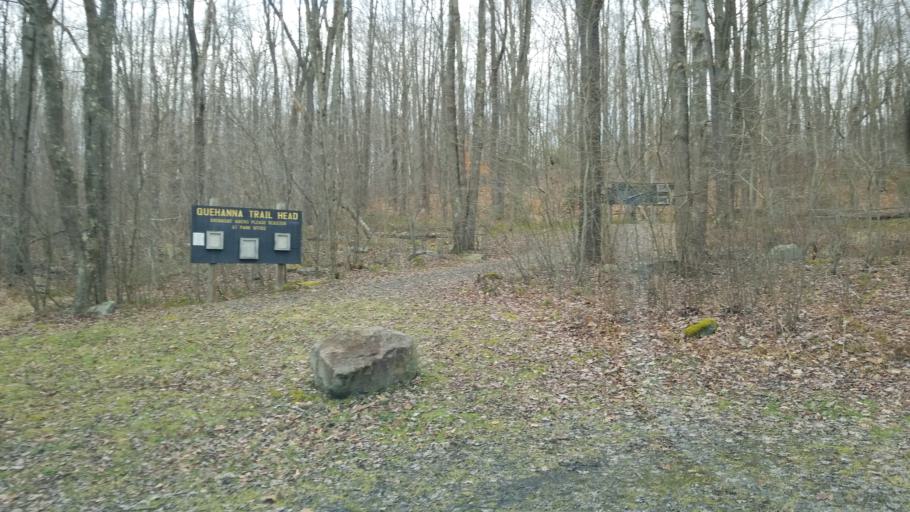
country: US
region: Pennsylvania
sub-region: Clearfield County
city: Clearfield
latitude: 41.1945
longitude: -78.5065
